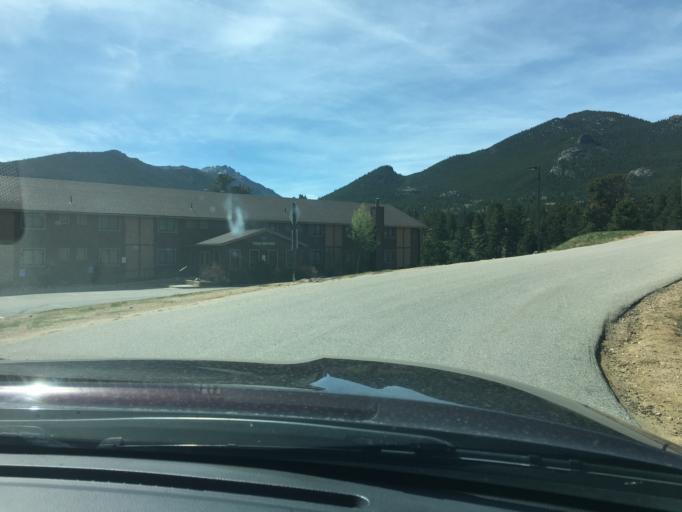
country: US
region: Colorado
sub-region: Larimer County
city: Estes Park
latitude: 40.3401
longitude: -105.5695
